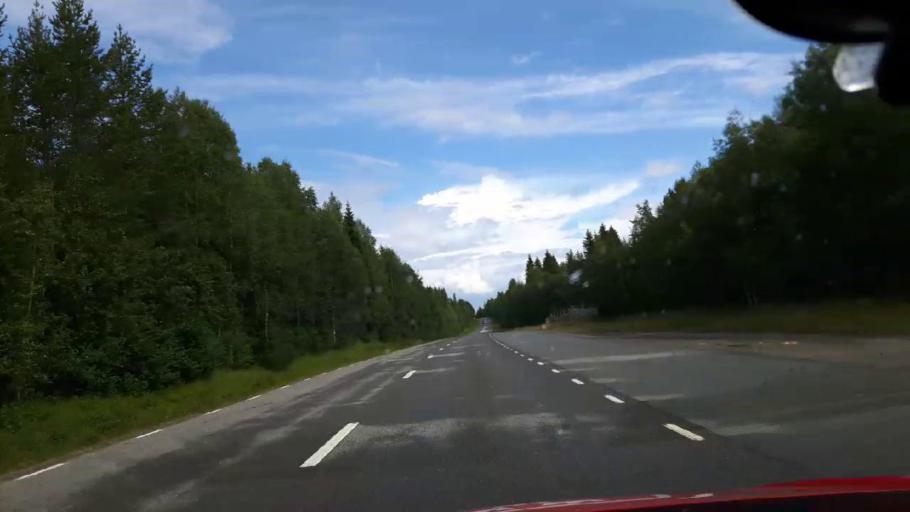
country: SE
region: Jaemtland
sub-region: Stroemsunds Kommun
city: Stroemsund
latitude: 64.3357
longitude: 14.9908
